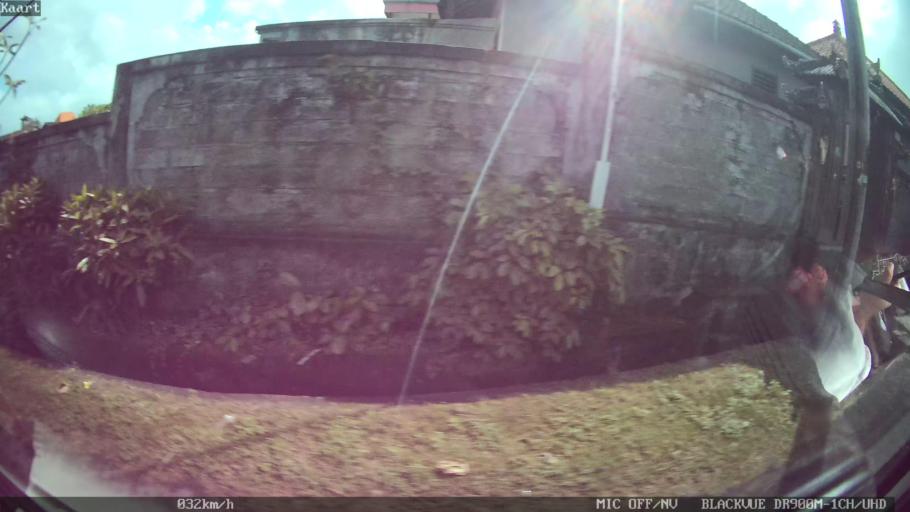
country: ID
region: Bali
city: Banjar Karangsuling
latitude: -8.5988
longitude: 115.2040
